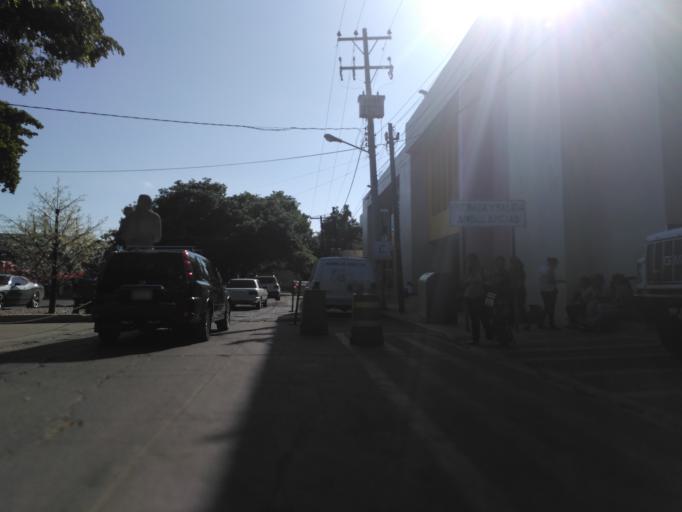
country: MX
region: Sinaloa
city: Culiacan
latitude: 24.7989
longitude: -107.3999
